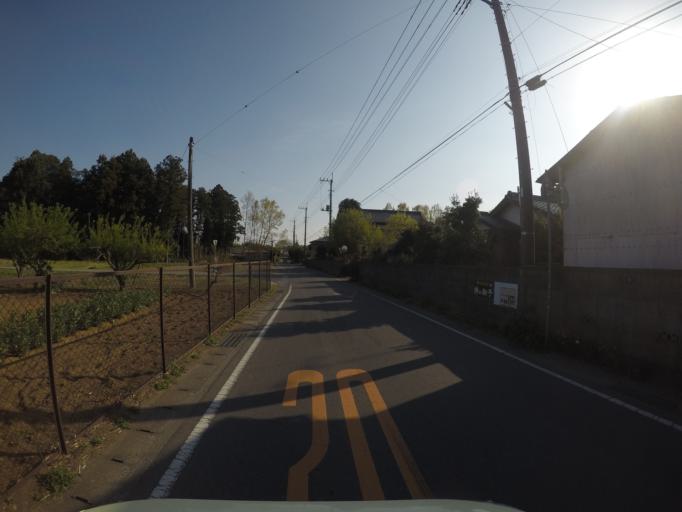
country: JP
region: Ibaraki
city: Ishige
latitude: 36.1714
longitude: 140.0173
